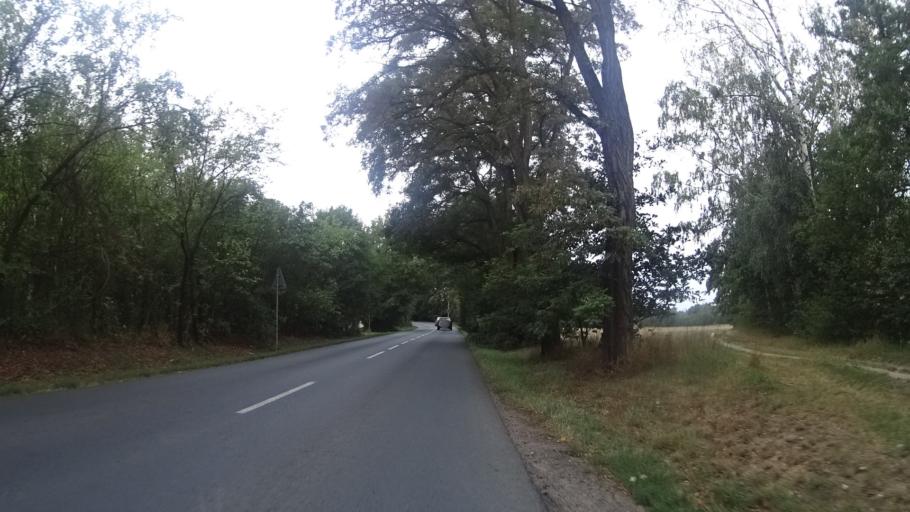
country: CZ
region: Kralovehradecky
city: Cernilov
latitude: 50.2073
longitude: 15.8961
